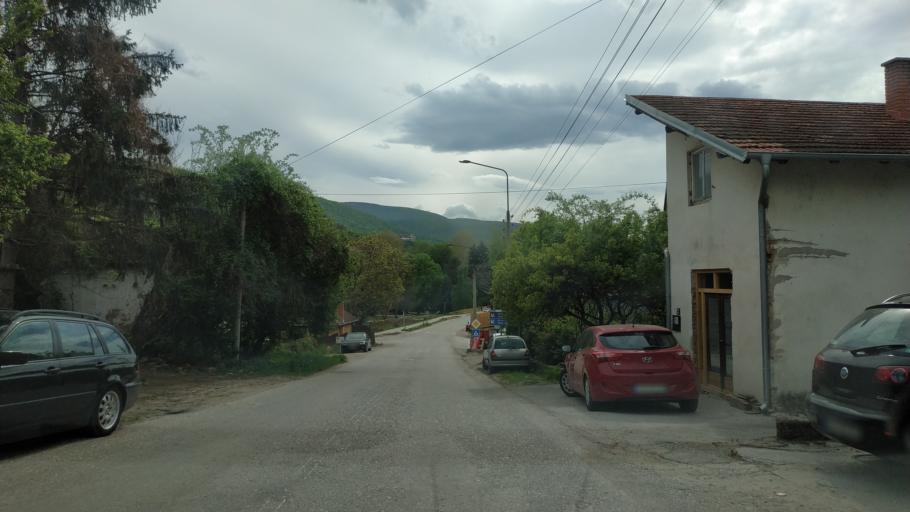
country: RS
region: Central Serbia
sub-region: Zajecarski Okrug
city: Soko Banja
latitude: 43.6460
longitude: 21.8828
